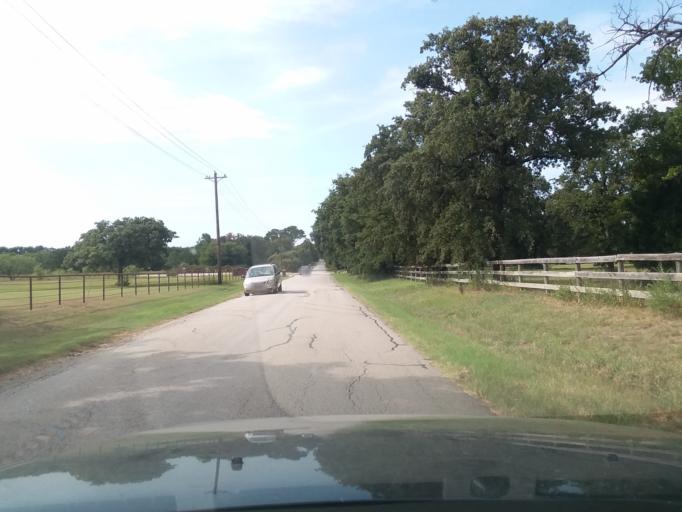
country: US
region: Texas
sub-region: Denton County
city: Copper Canyon
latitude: 33.1126
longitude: -97.1311
